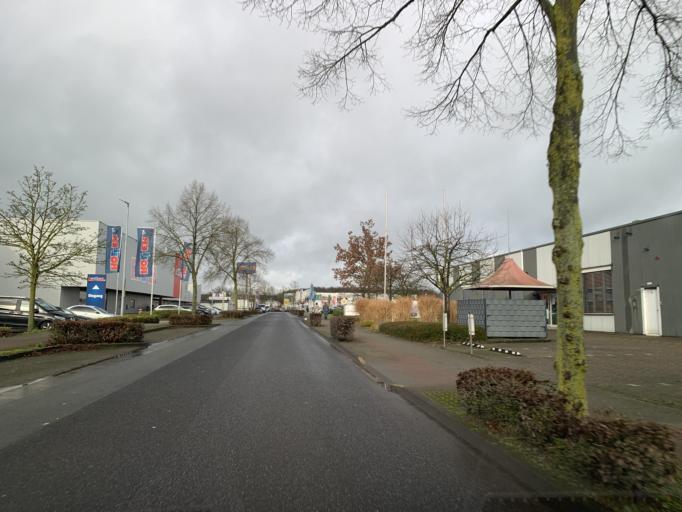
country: DE
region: North Rhine-Westphalia
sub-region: Regierungsbezirk Munster
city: Senden
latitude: 51.9096
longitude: 7.4854
